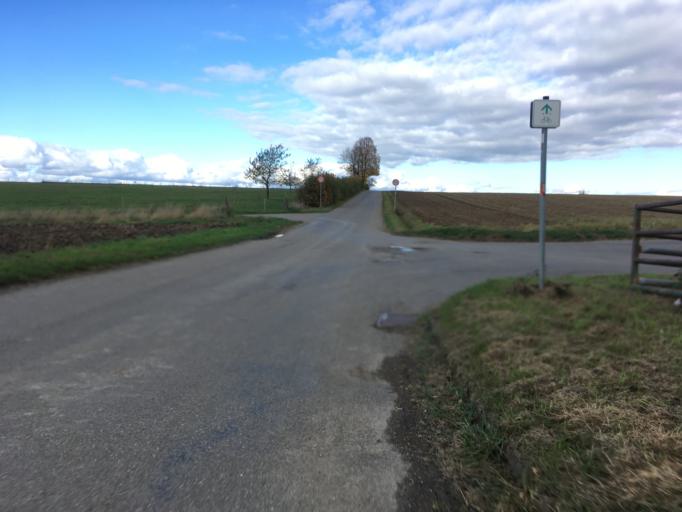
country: DE
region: Baden-Wuerttemberg
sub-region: Regierungsbezirk Stuttgart
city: Kupferzell
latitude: 49.2344
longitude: 9.7406
